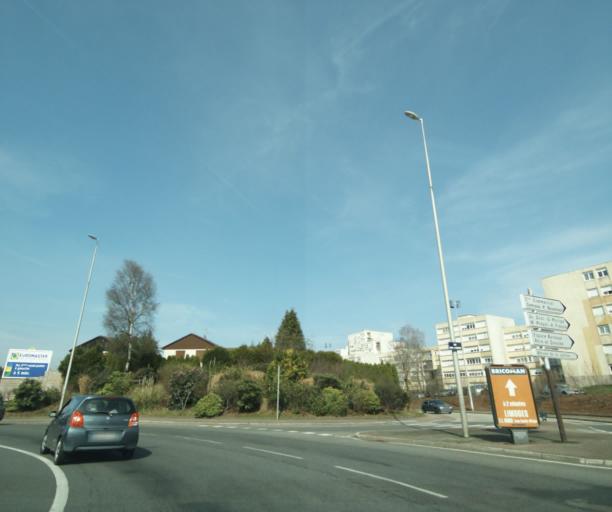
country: FR
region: Limousin
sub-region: Departement de la Haute-Vienne
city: Rilhac-Rancon
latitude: 45.8813
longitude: 1.2949
